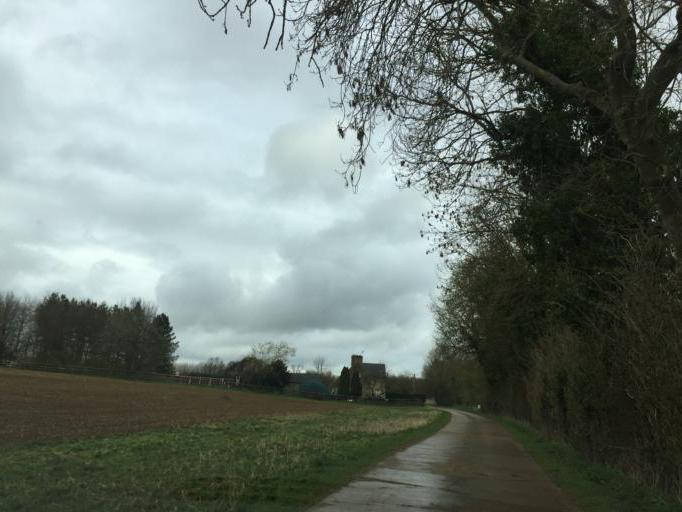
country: GB
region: England
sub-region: Oxfordshire
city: Woodstock
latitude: 51.9016
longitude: -1.3818
